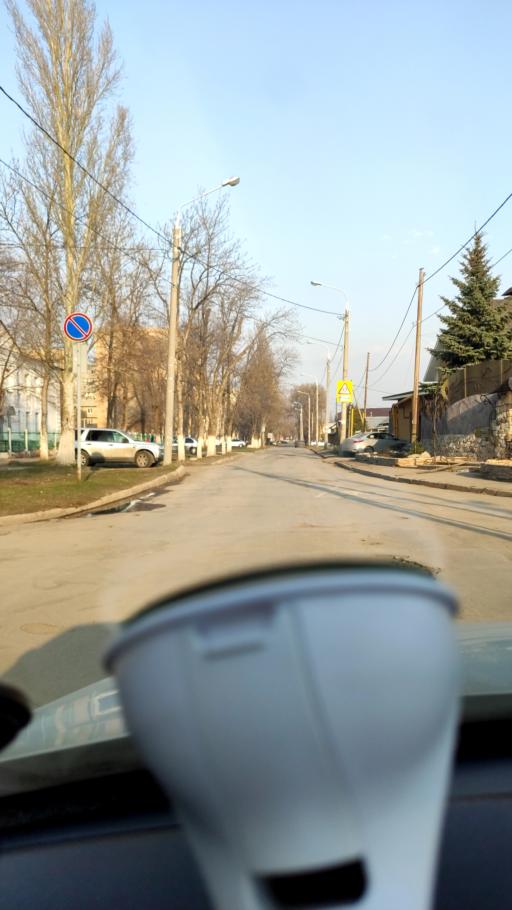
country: RU
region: Samara
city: Petra-Dubrava
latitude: 53.2967
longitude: 50.2786
